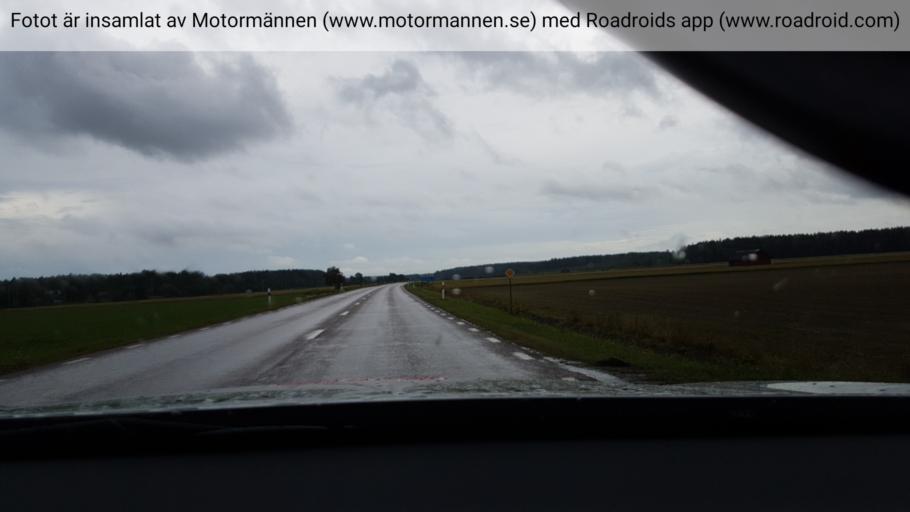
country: SE
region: Uppsala
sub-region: Tierps Kommun
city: Karlholmsbruk
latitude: 60.4627
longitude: 17.7663
